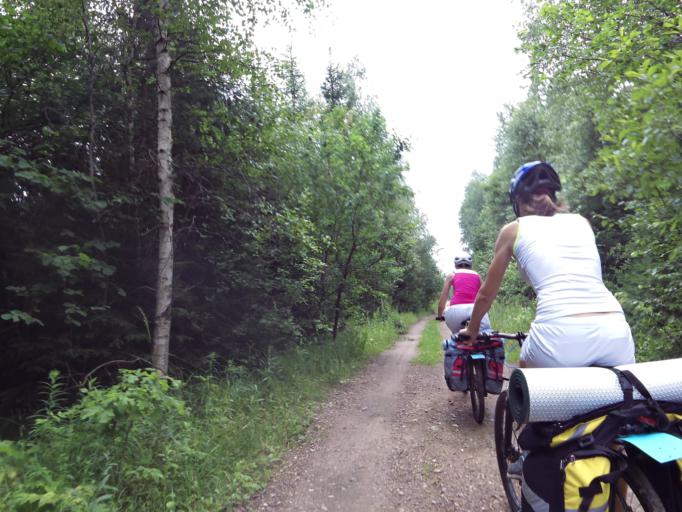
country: RU
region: Moskovskaya
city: Danki
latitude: 54.9474
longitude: 37.6924
